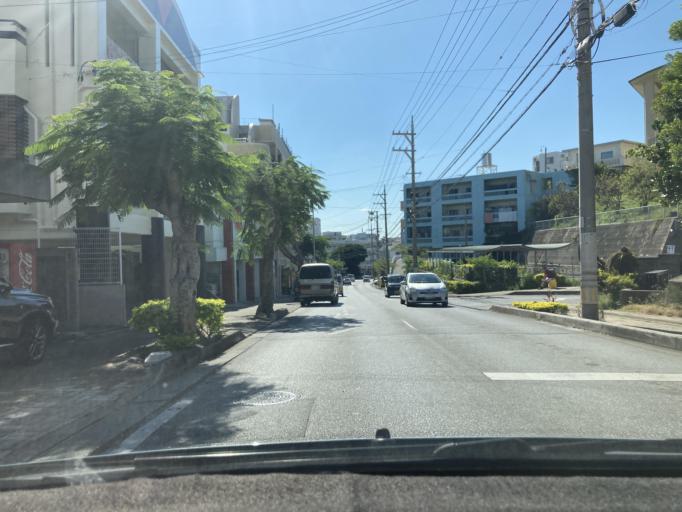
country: JP
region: Okinawa
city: Naha-shi
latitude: 26.2375
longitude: 127.7042
